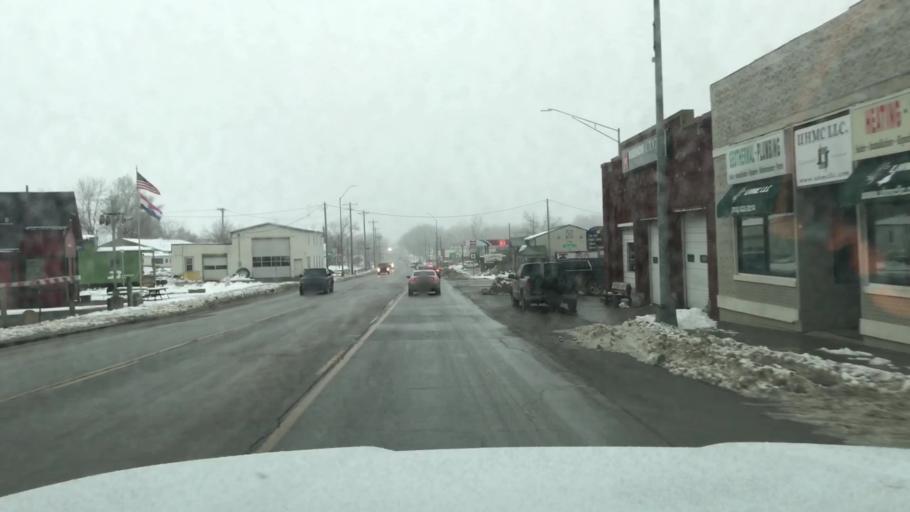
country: US
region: Missouri
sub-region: Clinton County
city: Cameron
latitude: 39.7408
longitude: -94.2359
